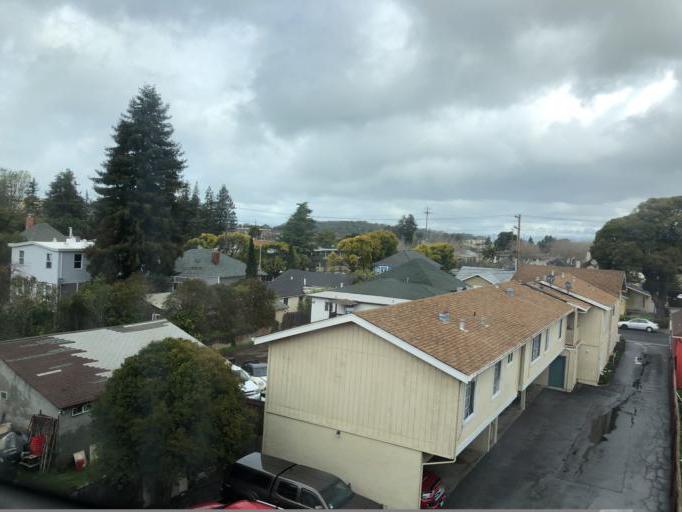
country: US
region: California
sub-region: San Mateo County
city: San Mateo
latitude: 37.5730
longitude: -122.3291
